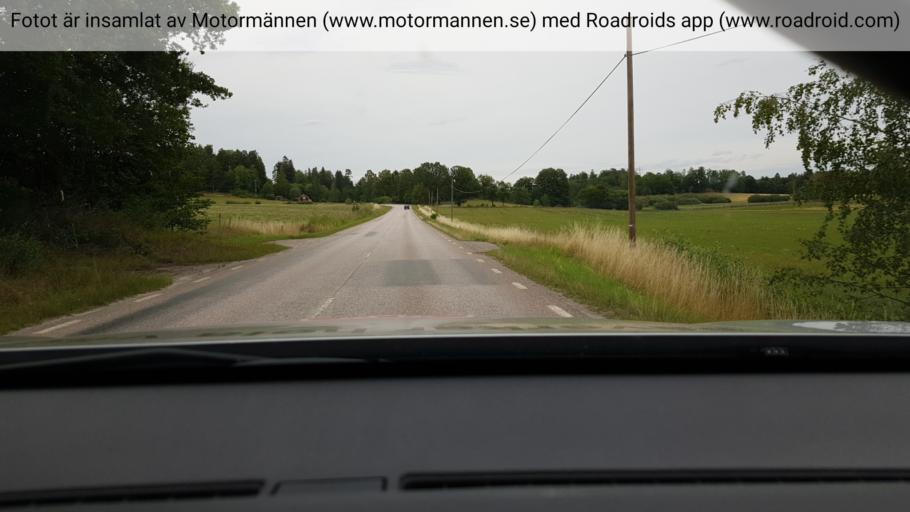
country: SE
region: Soedermanland
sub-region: Gnesta Kommun
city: Gnesta
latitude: 58.9939
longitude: 17.3364
